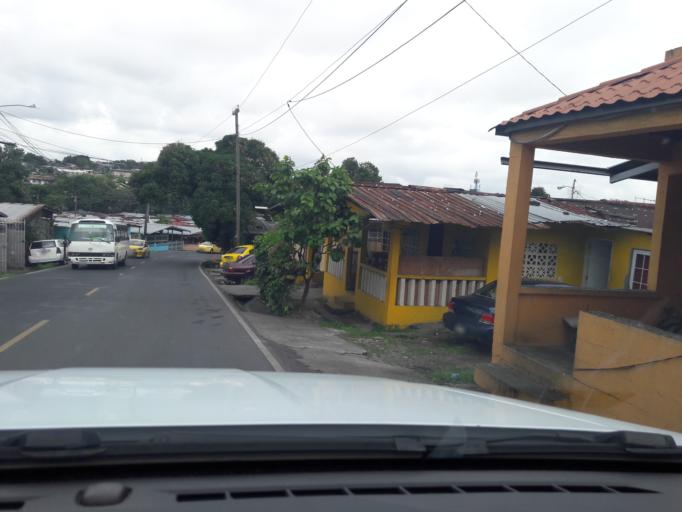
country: PA
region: Panama
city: San Miguelito
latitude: 9.0491
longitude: -79.5032
